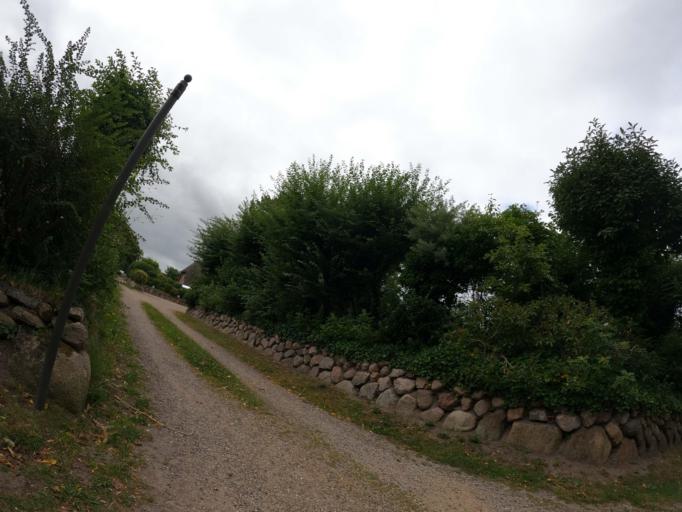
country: DE
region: Schleswig-Holstein
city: Tinnum
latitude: 54.9531
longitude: 8.3452
